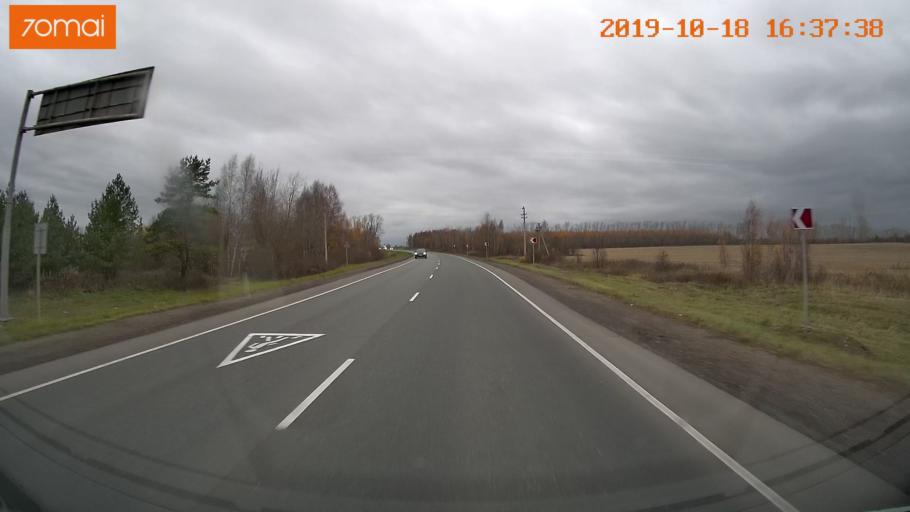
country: RU
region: Vladimir
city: Suzdal'
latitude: 56.4245
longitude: 40.4764
